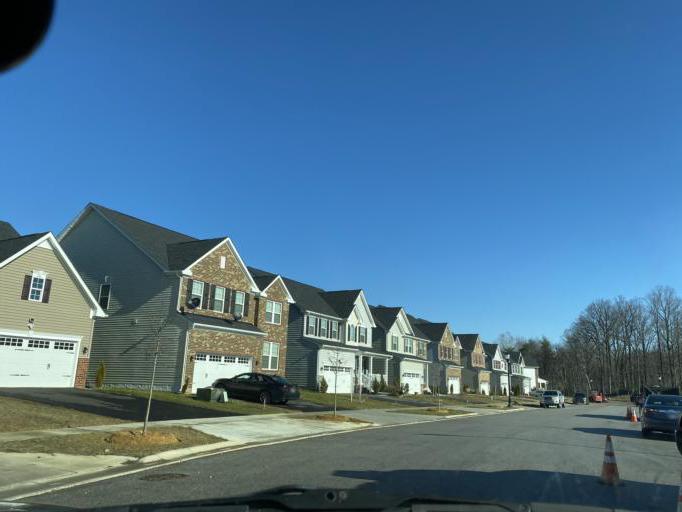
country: US
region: Maryland
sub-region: Montgomery County
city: Burtonsville
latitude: 39.0983
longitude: -76.9193
